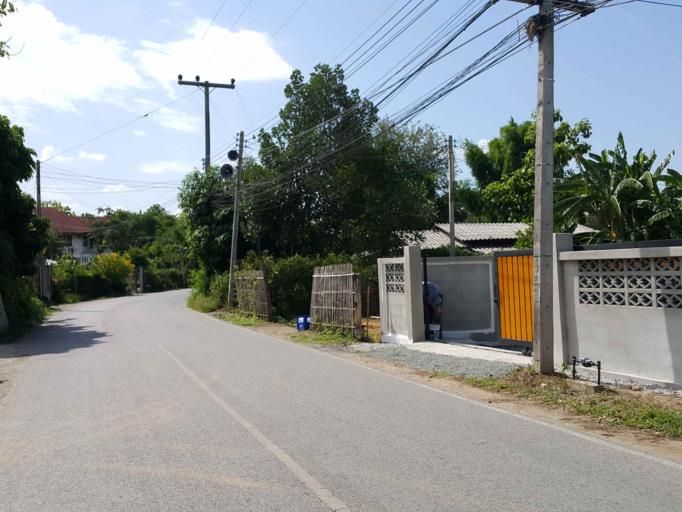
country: TH
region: Chiang Mai
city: San Kamphaeng
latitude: 18.7606
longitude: 99.1212
